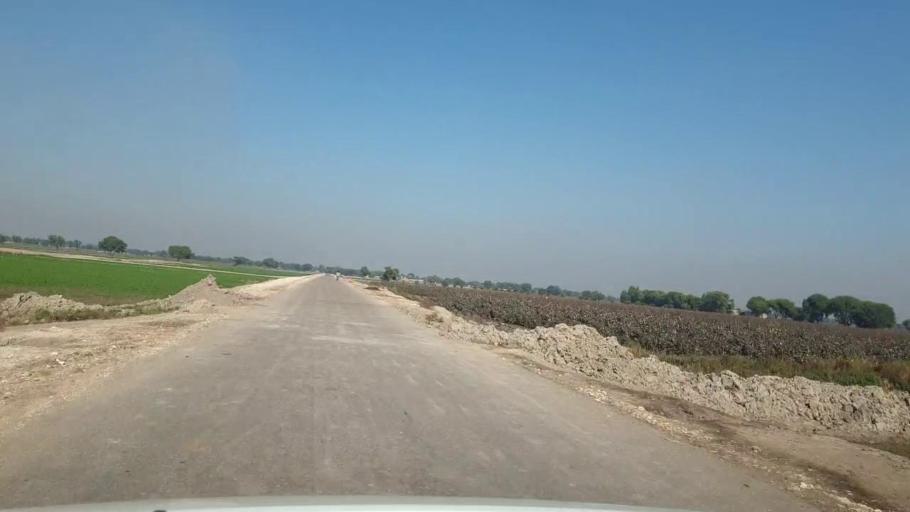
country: PK
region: Sindh
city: Bhan
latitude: 26.6559
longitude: 67.7061
